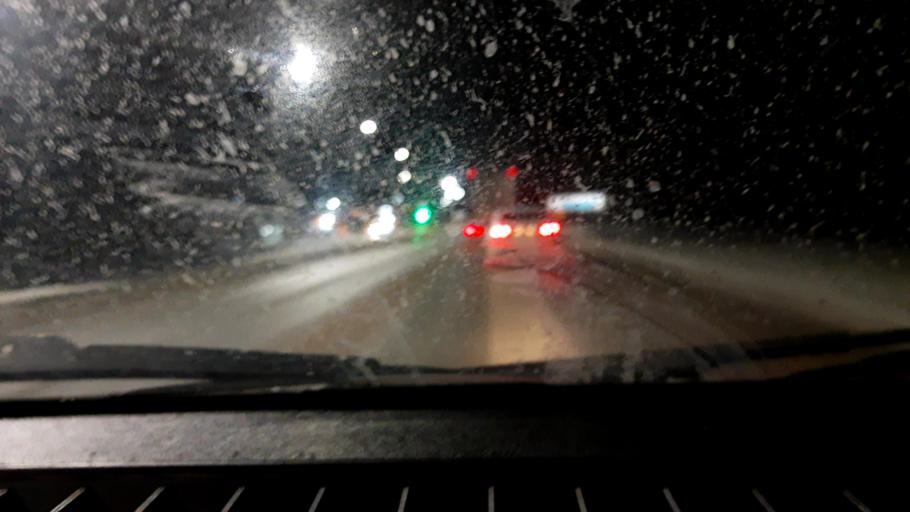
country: RU
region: Bashkortostan
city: Dyurtyuli
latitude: 55.4252
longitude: 54.8072
